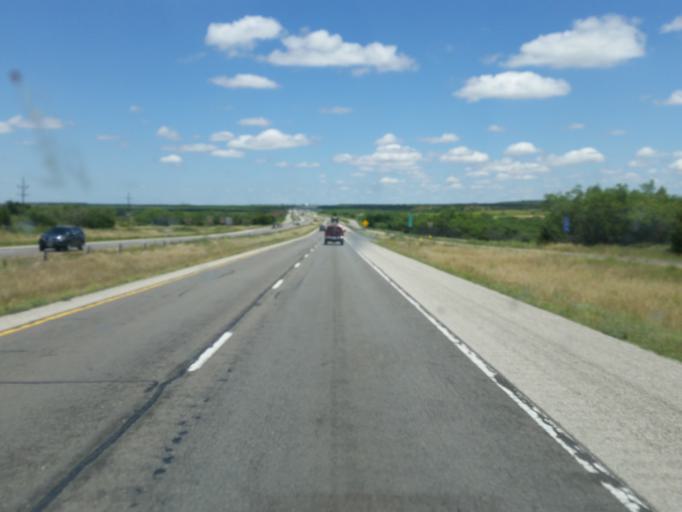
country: US
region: Texas
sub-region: Nolan County
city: Sweetwater
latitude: 32.4942
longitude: -100.2983
